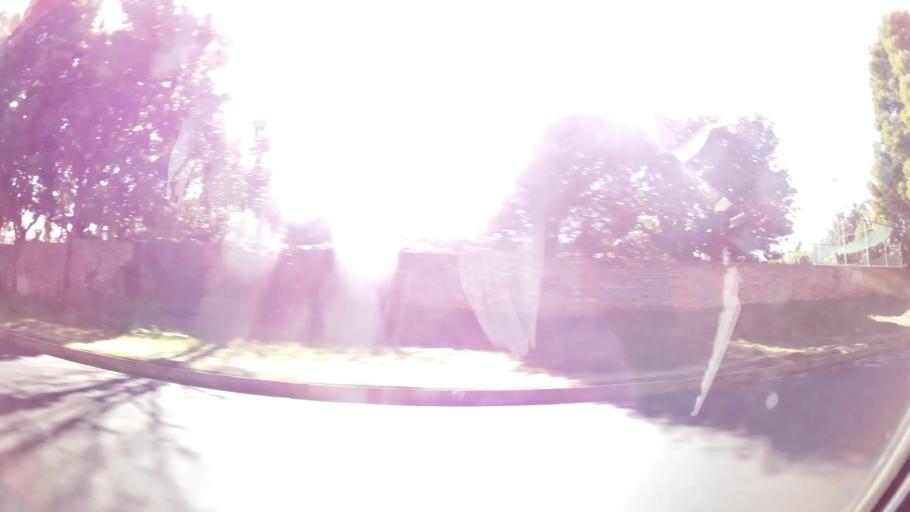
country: ZA
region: Gauteng
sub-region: City of Johannesburg Metropolitan Municipality
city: Roodepoort
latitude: -26.1309
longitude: 27.8887
